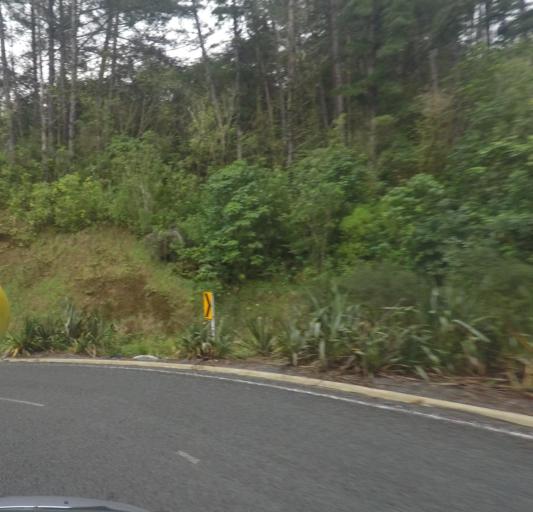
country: NZ
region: Auckland
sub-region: Auckland
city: Warkworth
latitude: -36.3743
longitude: 174.8021
